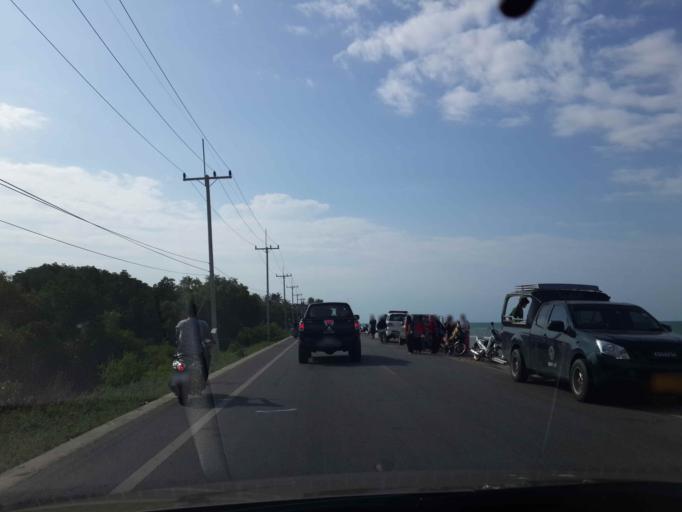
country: TH
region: Pattani
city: Yaring
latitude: 6.9265
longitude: 101.3266
